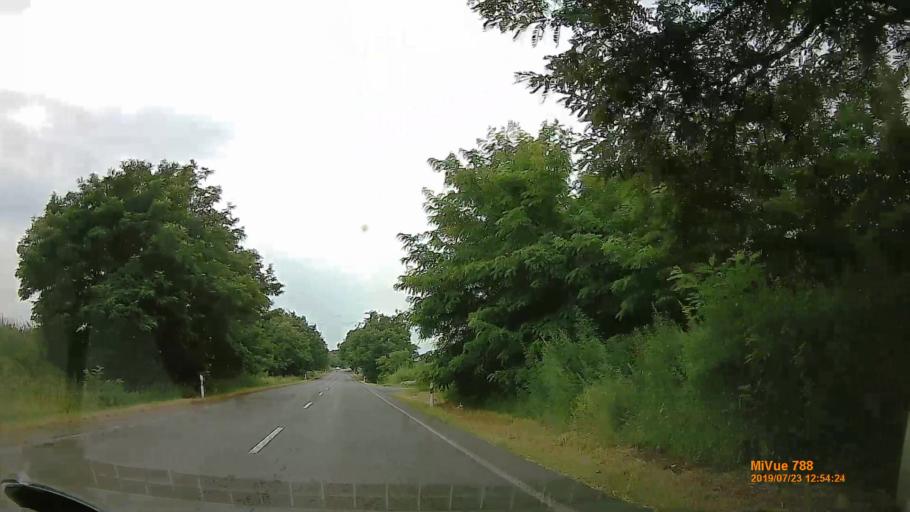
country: HU
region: Szabolcs-Szatmar-Bereg
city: Nagycserkesz
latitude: 47.9617
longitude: 21.5393
